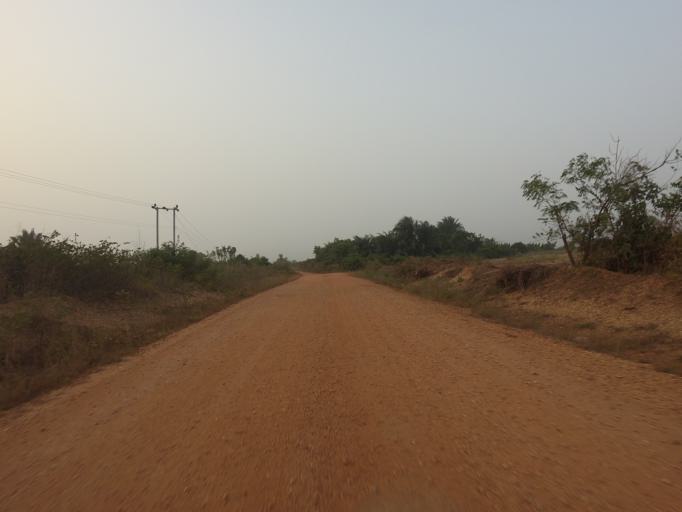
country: GH
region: Volta
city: Anloga
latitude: 5.9788
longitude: 0.6056
